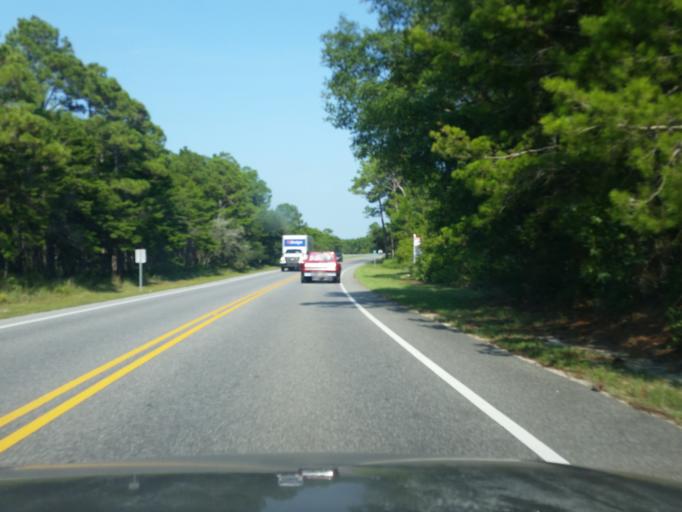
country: US
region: Alabama
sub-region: Baldwin County
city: Gulf Shores
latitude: 30.2528
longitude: -87.7497
